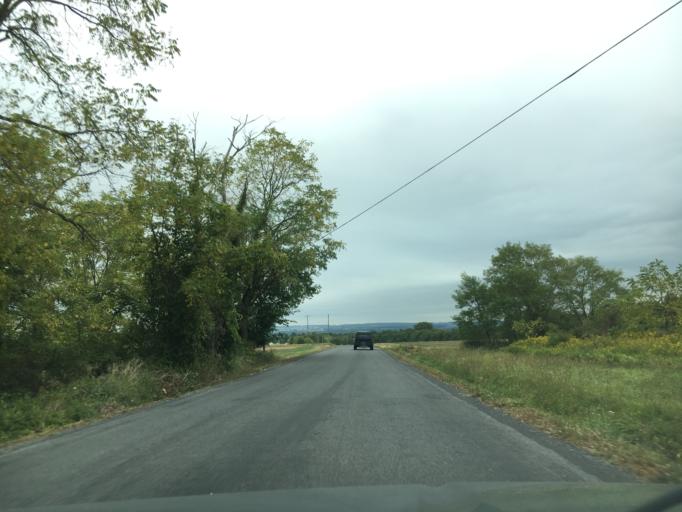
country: US
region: New York
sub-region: Tompkins County
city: Trumansburg
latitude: 42.6724
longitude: -76.7481
